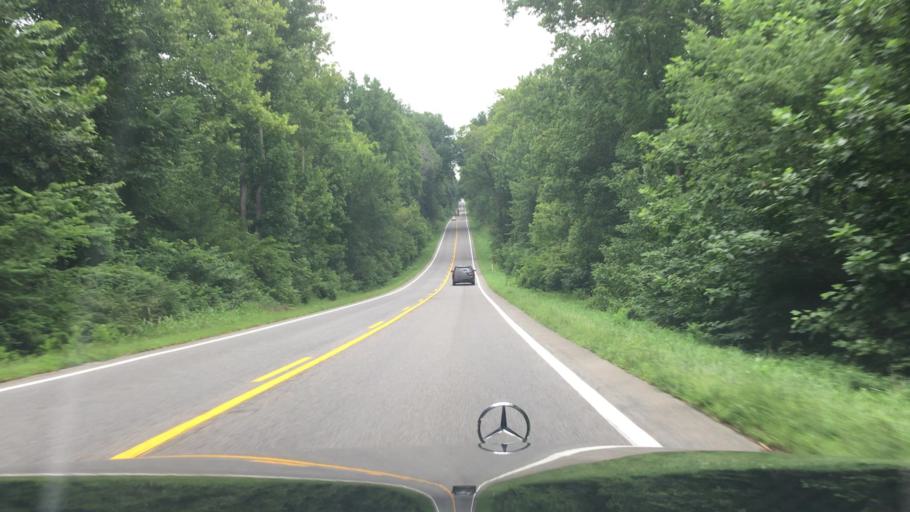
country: US
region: Virginia
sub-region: Prince Edward County
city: Farmville
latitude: 37.2733
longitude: -78.2745
